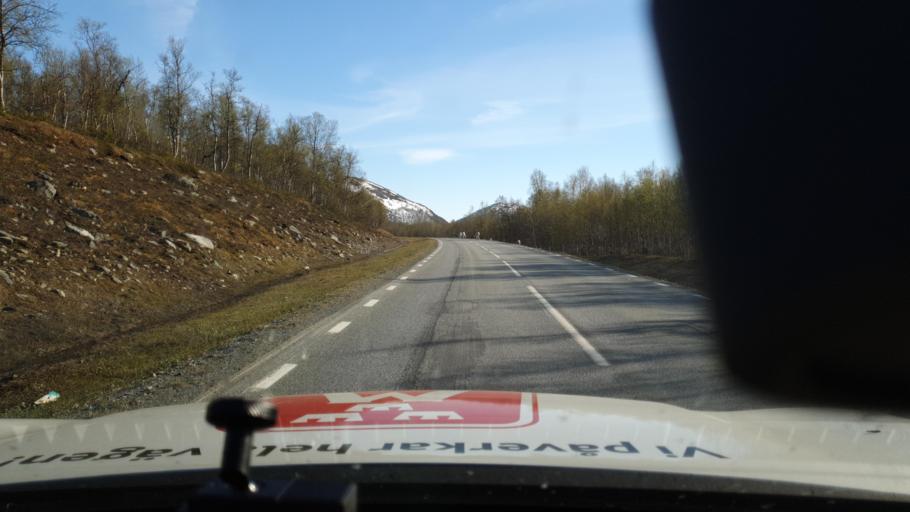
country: NO
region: Nordland
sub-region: Rana
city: Mo i Rana
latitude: 65.9894
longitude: 15.0692
